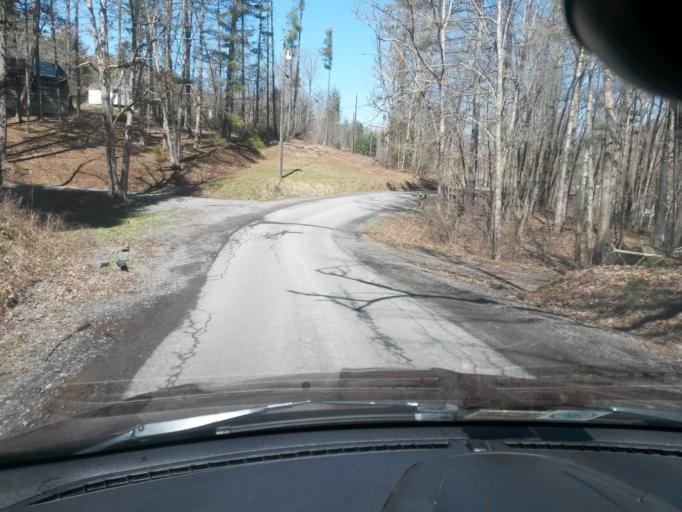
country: US
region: West Virginia
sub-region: Greenbrier County
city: White Sulphur Springs
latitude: 37.6464
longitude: -80.3296
